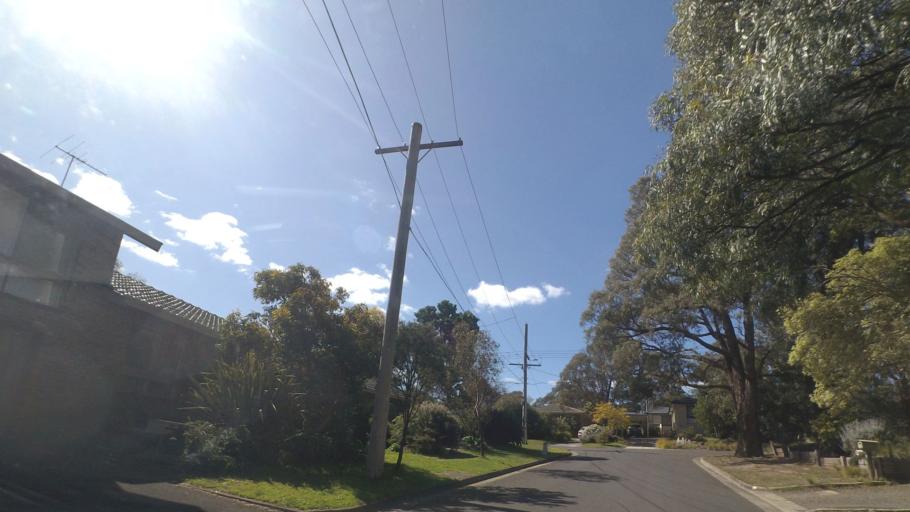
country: AU
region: Victoria
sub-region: Maroondah
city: Heathmont
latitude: -37.8349
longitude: 145.2380
